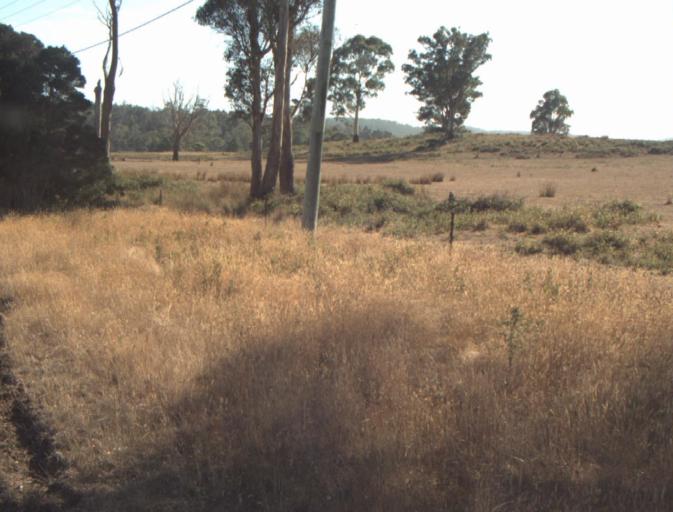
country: AU
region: Tasmania
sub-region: Dorset
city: Bridport
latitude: -41.1439
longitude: 147.2122
